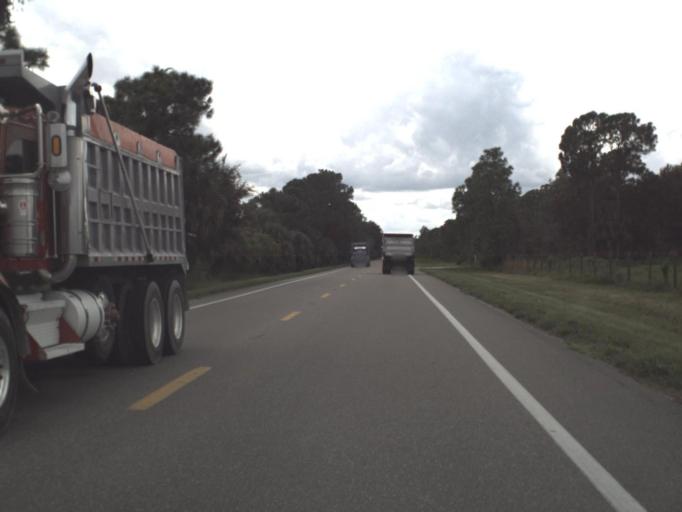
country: US
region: Florida
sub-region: DeSoto County
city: Nocatee
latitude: 26.9761
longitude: -81.7606
